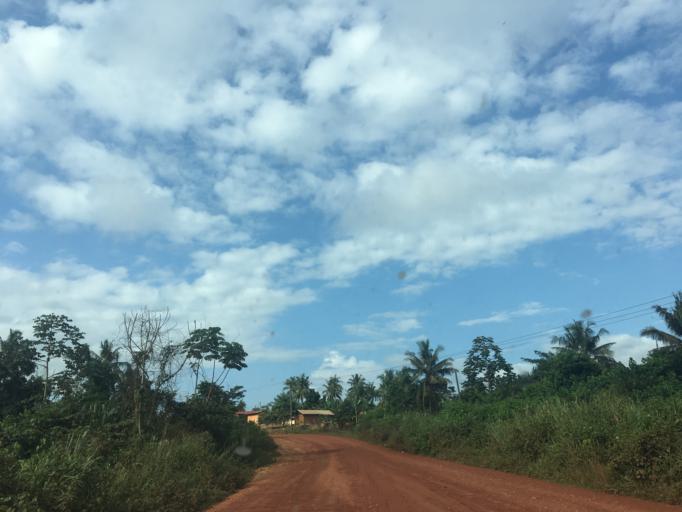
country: GH
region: Western
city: Wassa-Akropong
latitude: 5.9573
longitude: -2.4318
